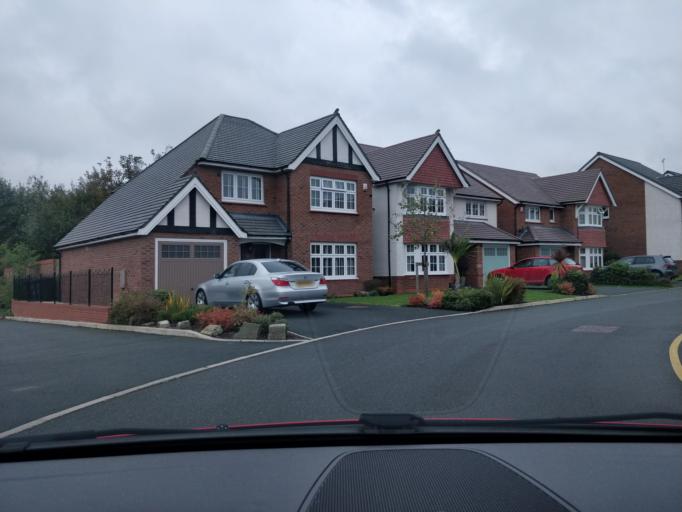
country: GB
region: England
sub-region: Lancashire
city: Ormskirk
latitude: 53.5670
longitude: -2.8771
